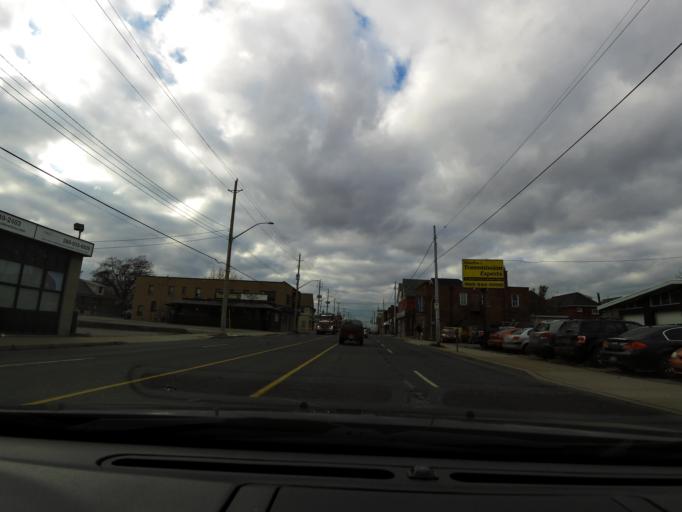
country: CA
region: Ontario
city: Hamilton
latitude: 43.2534
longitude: -79.8241
